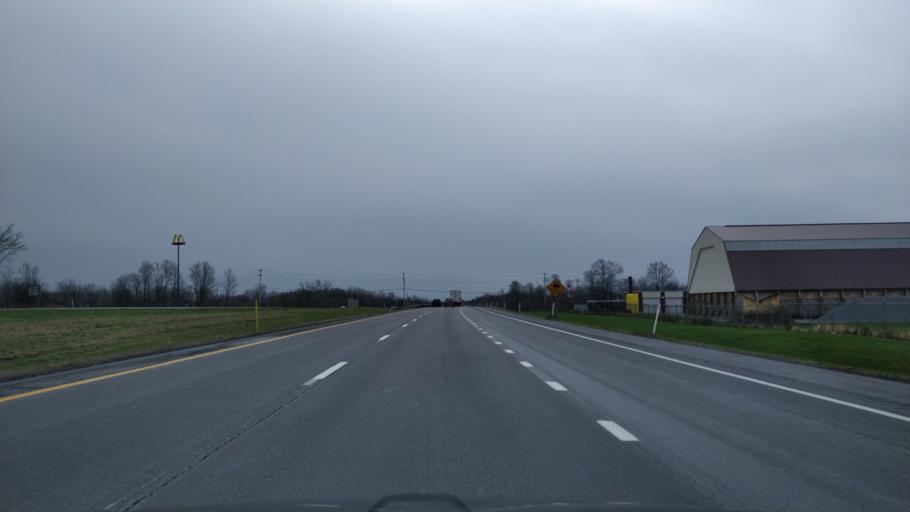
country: US
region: New York
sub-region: Jefferson County
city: Adams
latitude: 43.8141
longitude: -76.0337
